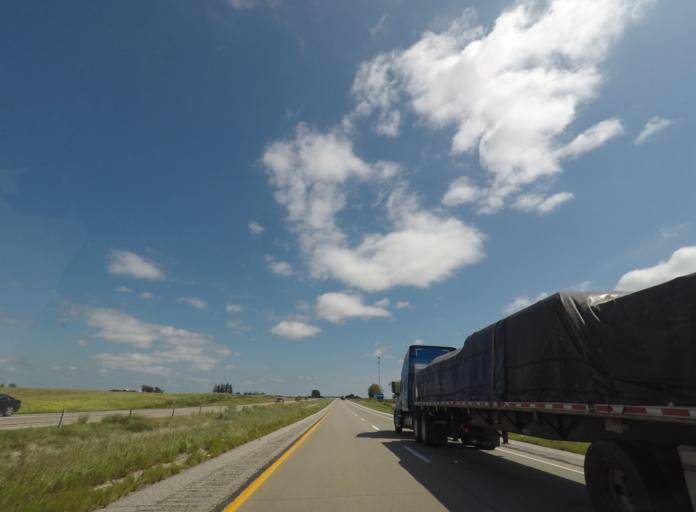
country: US
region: Iowa
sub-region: Iowa County
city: Williamsburg
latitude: 41.6870
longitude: -91.9784
